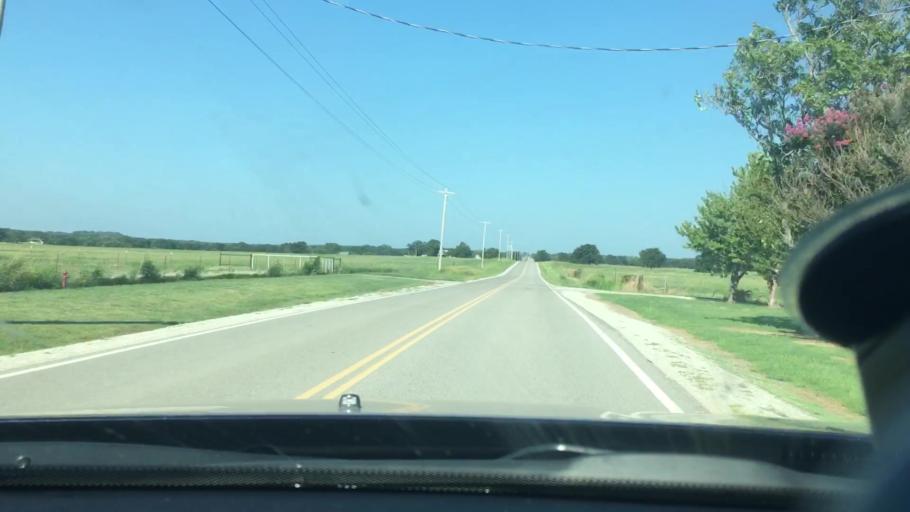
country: US
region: Oklahoma
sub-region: Love County
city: Marietta
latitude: 34.0275
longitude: -97.1753
